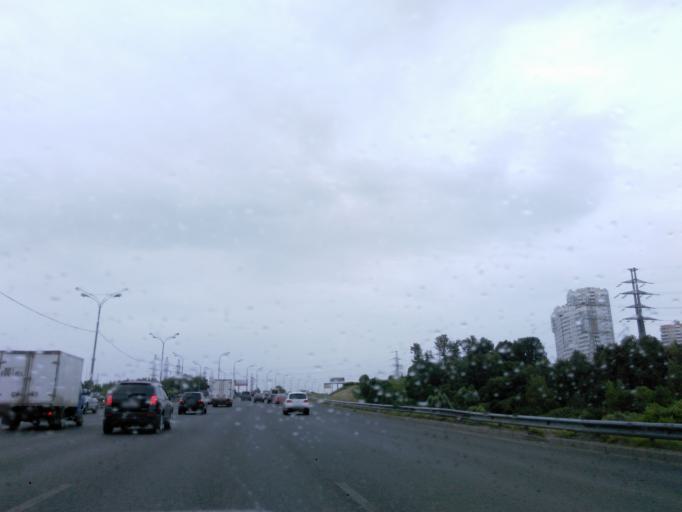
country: RU
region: Moscow
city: Strogino
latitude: 55.8423
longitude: 37.3935
